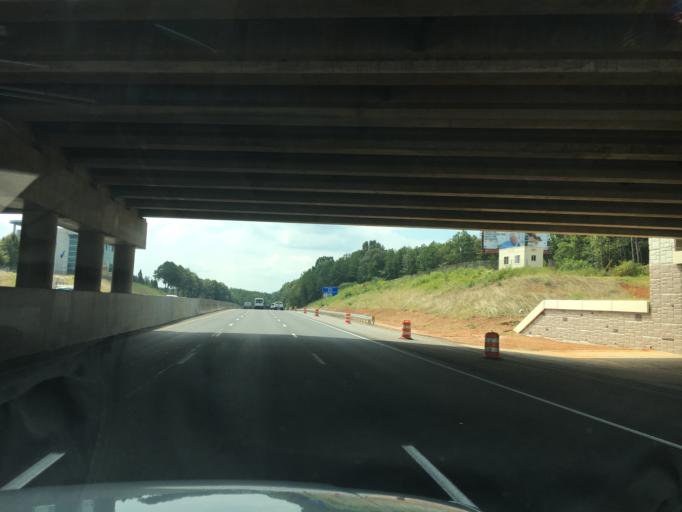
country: US
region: South Carolina
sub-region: Greenville County
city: Mauldin
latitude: 34.8209
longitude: -82.3173
